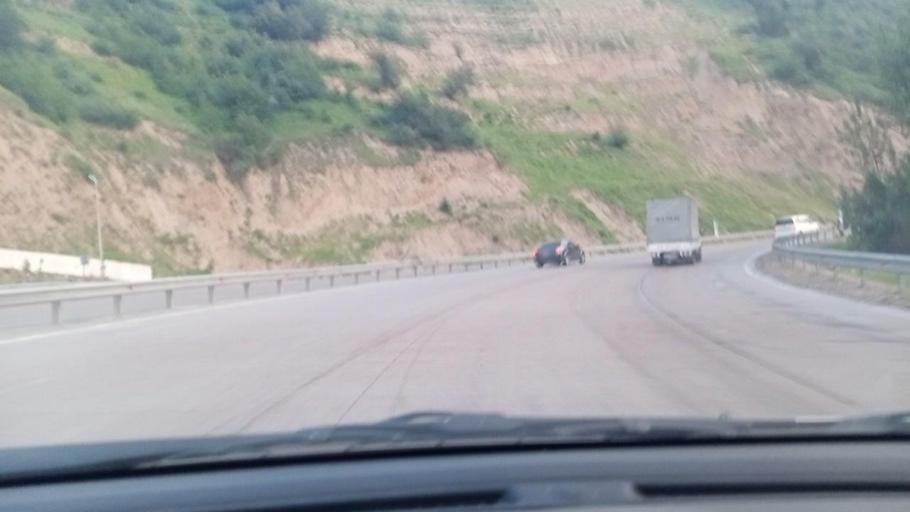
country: UZ
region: Toshkent
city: Angren
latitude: 41.1549
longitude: 70.4482
